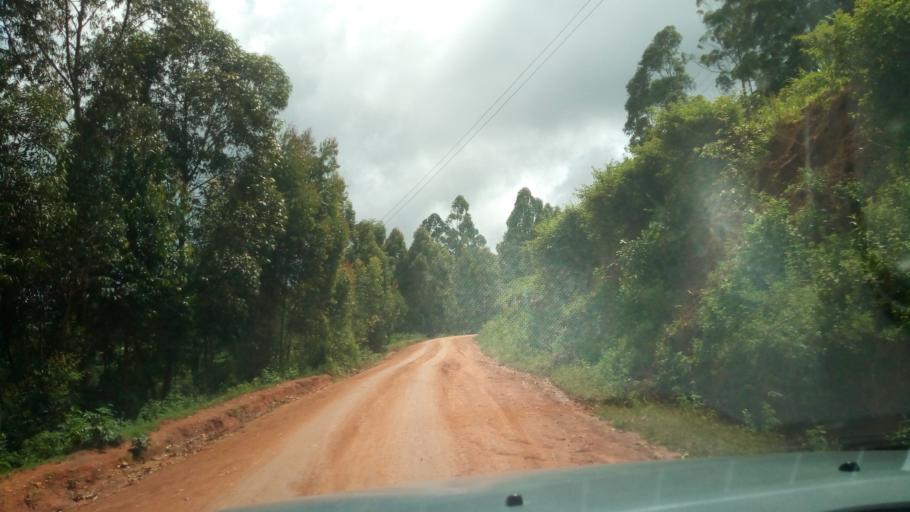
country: KE
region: Makueni
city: Wote
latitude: -1.6715
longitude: 37.4500
